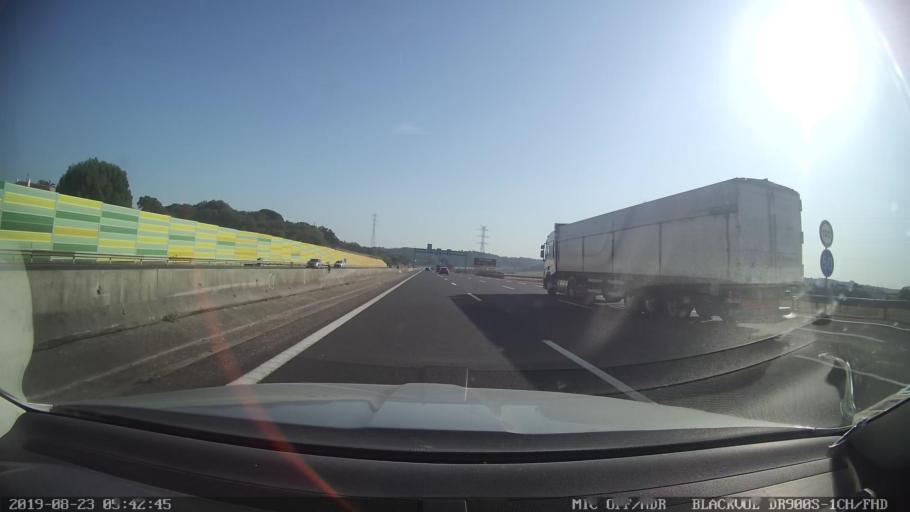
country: PT
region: Santarem
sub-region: Santarem
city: Santarem
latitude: 39.2552
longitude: -8.7371
